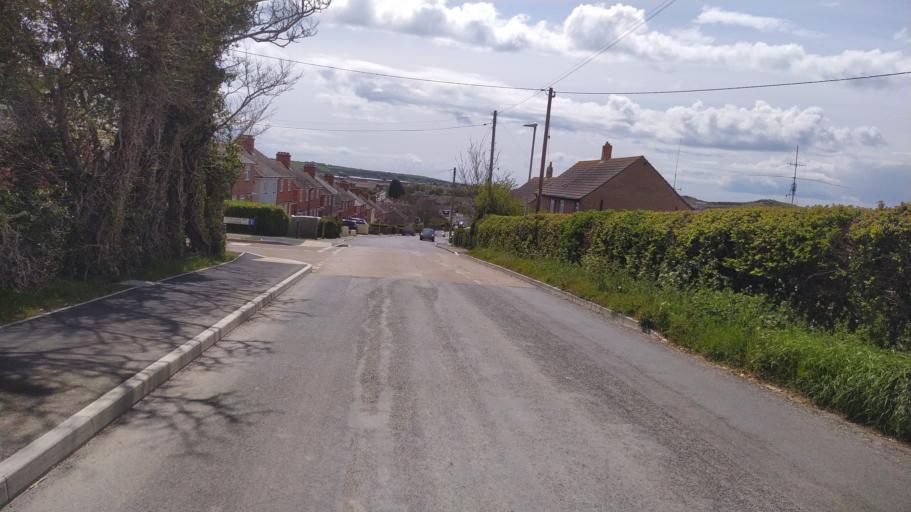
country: GB
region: England
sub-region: Dorset
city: Chickerell
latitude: 50.6267
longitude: -2.4988
